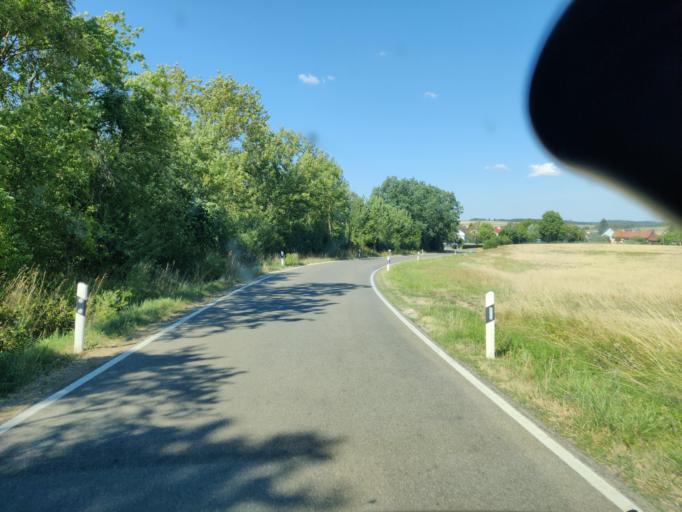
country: DE
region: Bavaria
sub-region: Regierungsbezirk Mittelfranken
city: Ettenstatt
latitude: 49.0757
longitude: 11.0628
